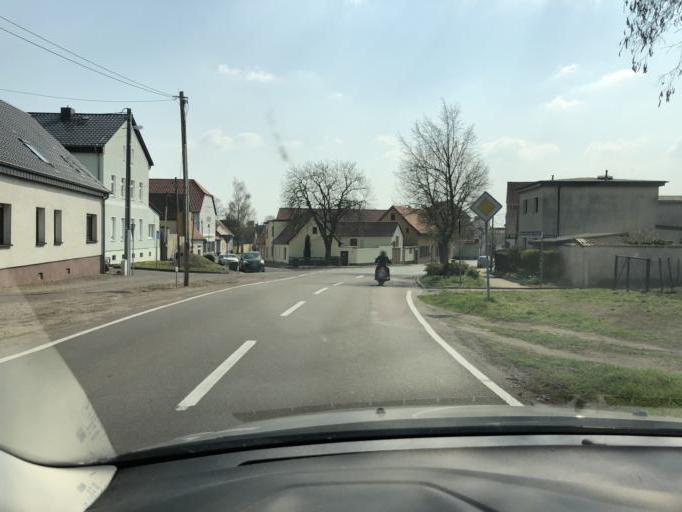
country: DE
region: Saxony-Anhalt
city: Oppin
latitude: 51.5724
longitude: 12.0519
